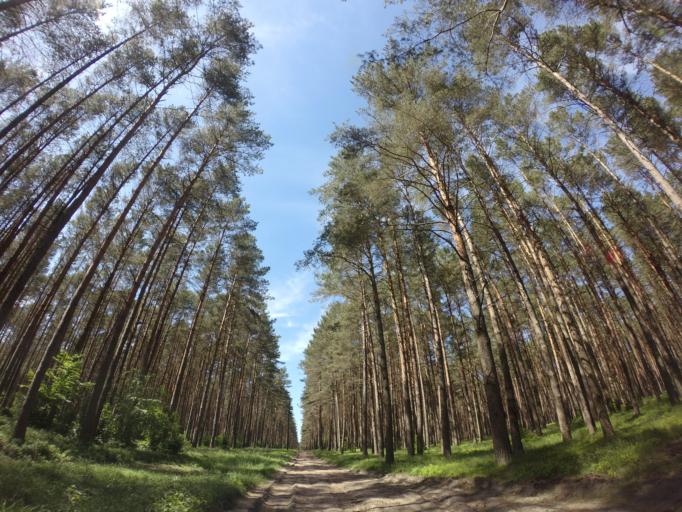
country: PL
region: West Pomeranian Voivodeship
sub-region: Powiat choszczenski
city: Drawno
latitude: 53.1232
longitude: 15.8007
